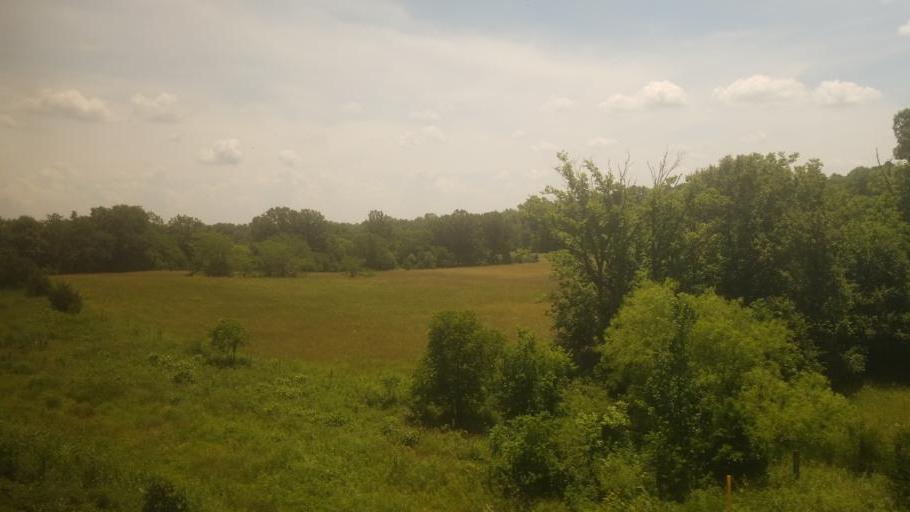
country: US
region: Missouri
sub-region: Linn County
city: Marceline
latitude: 39.8672
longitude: -92.7916
